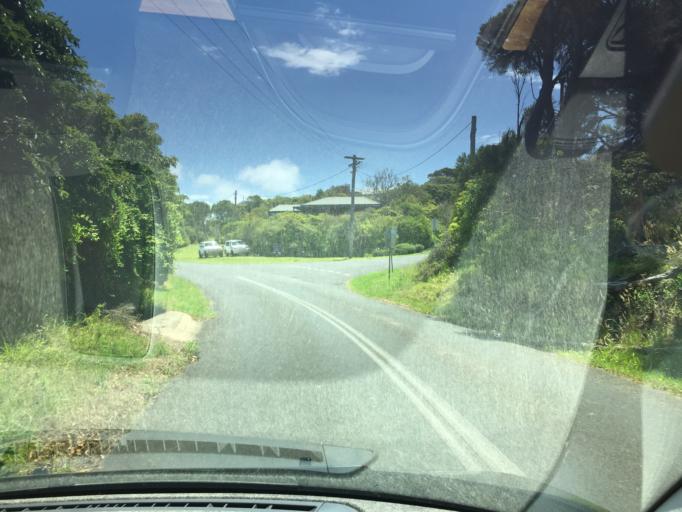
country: AU
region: New South Wales
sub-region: Bega Valley
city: Merimbula
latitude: -36.8975
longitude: 149.9269
